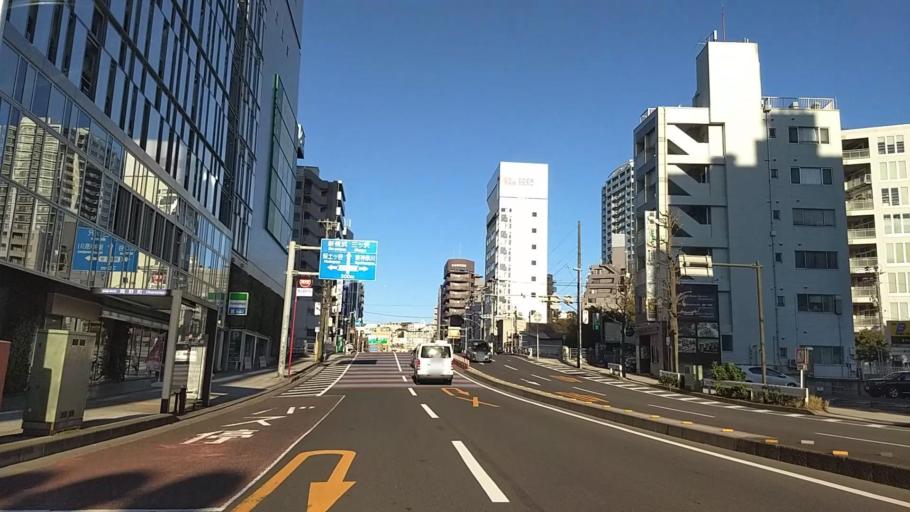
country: JP
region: Kanagawa
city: Yokohama
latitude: 35.4638
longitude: 139.6149
